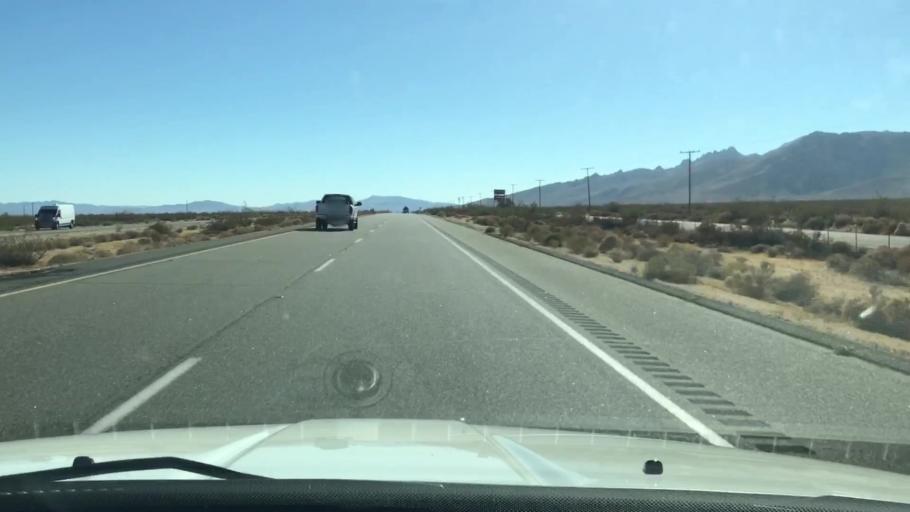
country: US
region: California
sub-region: Kern County
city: Inyokern
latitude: 35.7823
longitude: -117.8721
